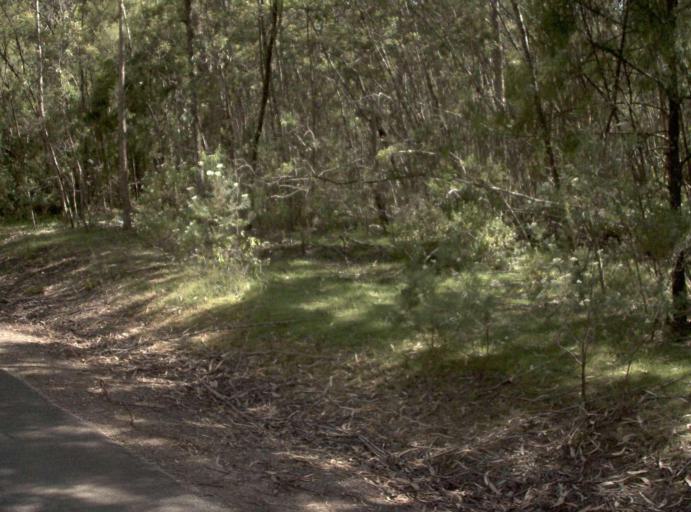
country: AU
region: Victoria
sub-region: East Gippsland
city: Lakes Entrance
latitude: -37.4358
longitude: 148.1304
